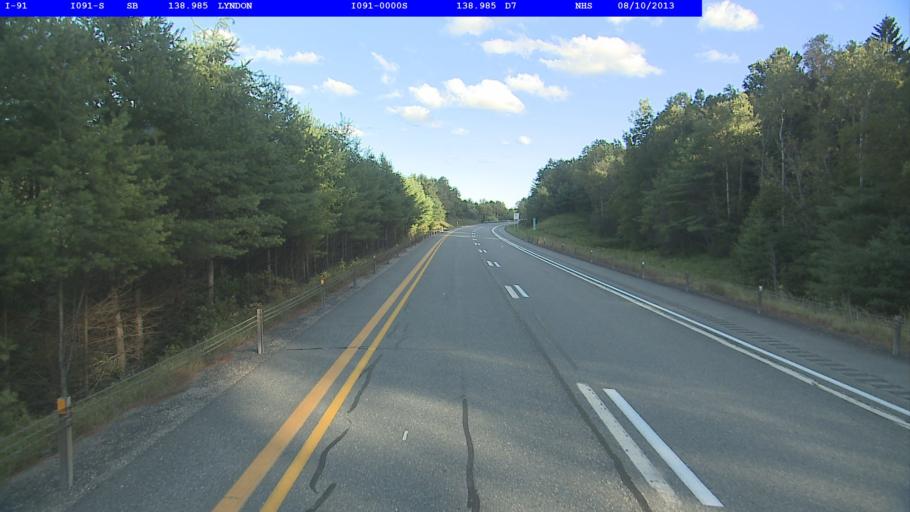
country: US
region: Vermont
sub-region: Caledonia County
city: Lyndonville
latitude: 44.5415
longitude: -72.0219
